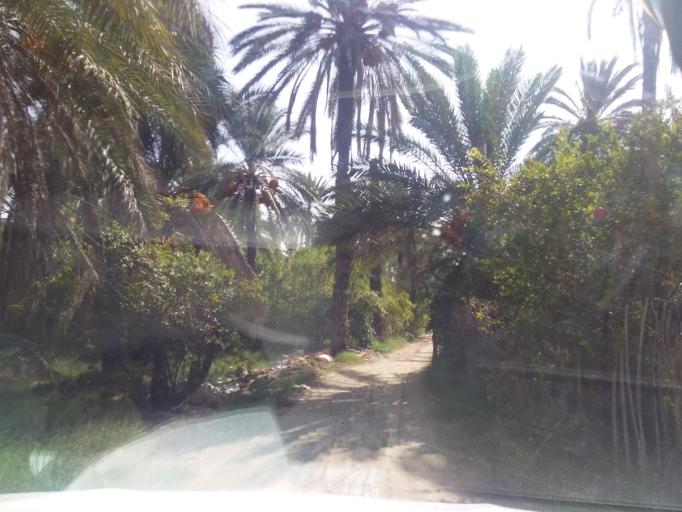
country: TN
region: Qabis
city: Gabes
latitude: 33.6254
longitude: 10.2876
